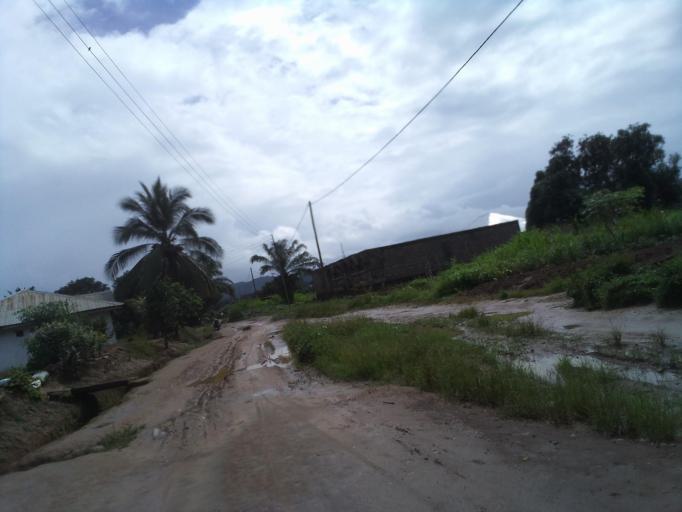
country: SL
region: Eastern Province
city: Kenema
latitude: 7.8499
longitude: -11.1980
